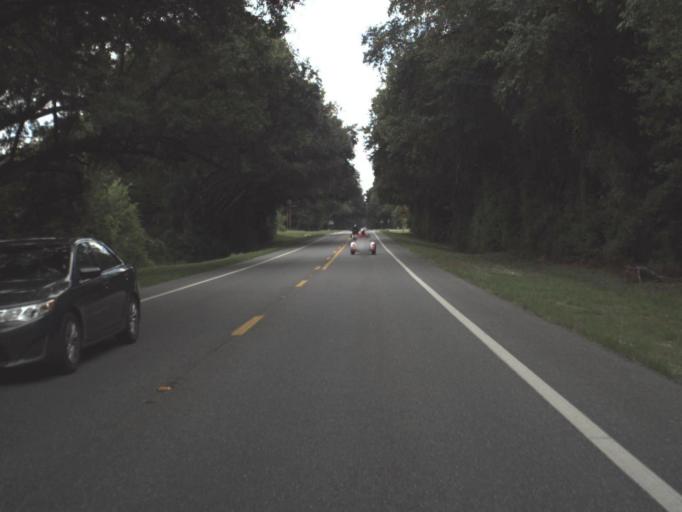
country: US
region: Florida
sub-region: Alachua County
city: Newberry
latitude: 29.6124
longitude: -82.5891
